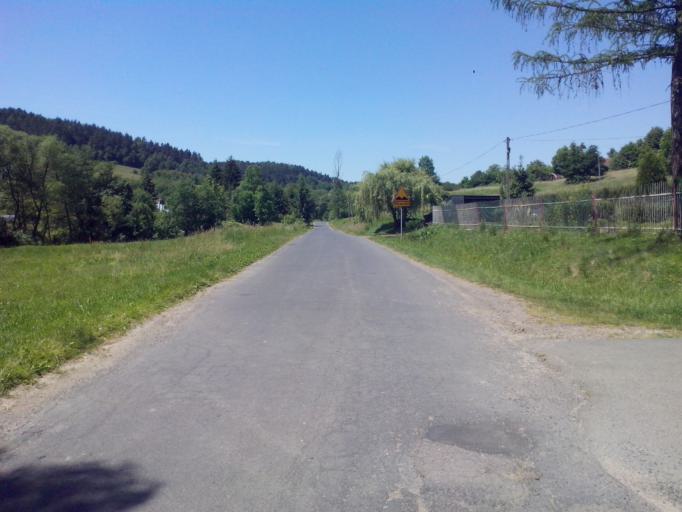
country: PL
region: Subcarpathian Voivodeship
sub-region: Powiat krosnienski
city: Wojaszowka
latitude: 49.8008
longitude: 21.7008
